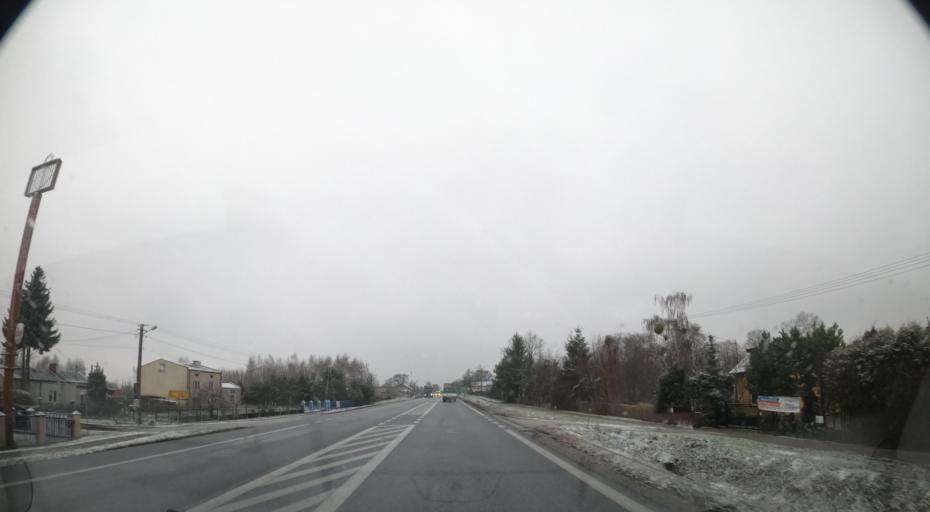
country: PL
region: Masovian Voivodeship
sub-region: Powiat sochaczewski
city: Paprotnia
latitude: 52.2114
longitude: 20.4360
